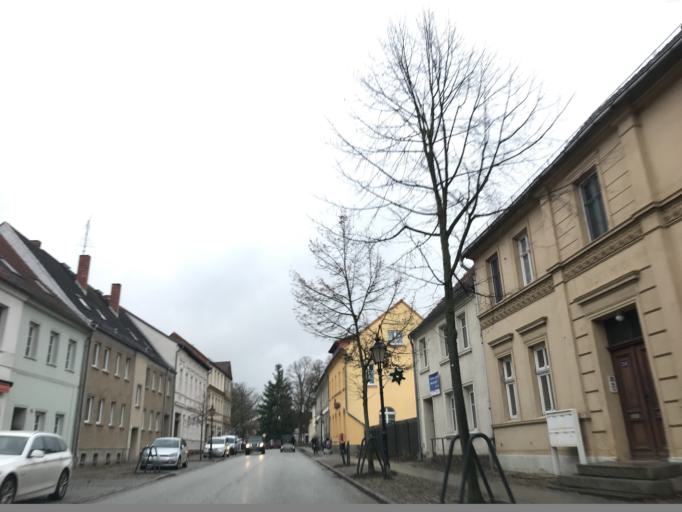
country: DE
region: Brandenburg
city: Lindow
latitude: 52.9723
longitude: 12.9881
